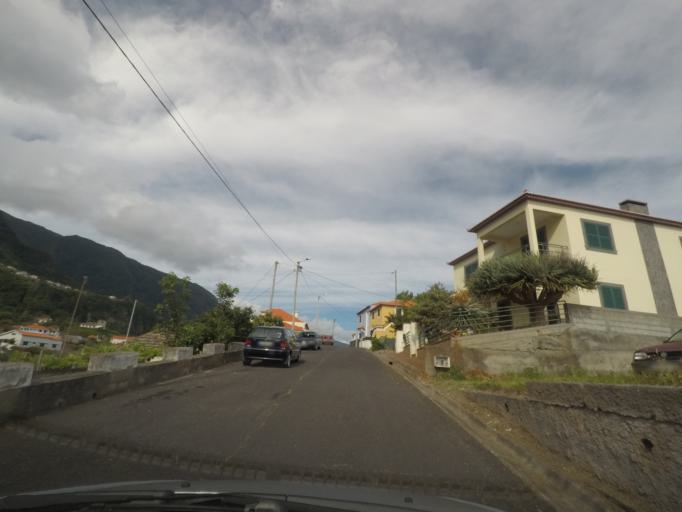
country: PT
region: Madeira
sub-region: Sao Vicente
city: Sao Vicente
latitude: 32.8270
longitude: -16.9891
